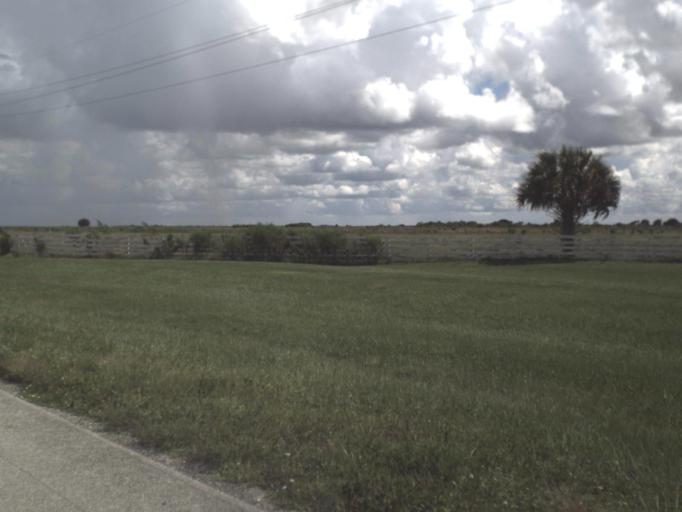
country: US
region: Florida
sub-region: Highlands County
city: Placid Lakes
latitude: 27.2096
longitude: -81.6173
